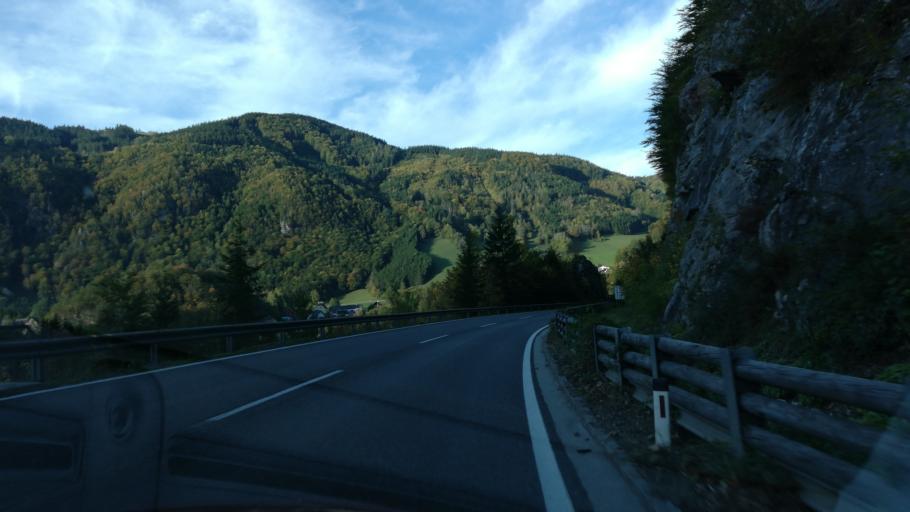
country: AT
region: Upper Austria
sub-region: Politischer Bezirk Steyr-Land
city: Weyer
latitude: 47.8489
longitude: 14.6398
